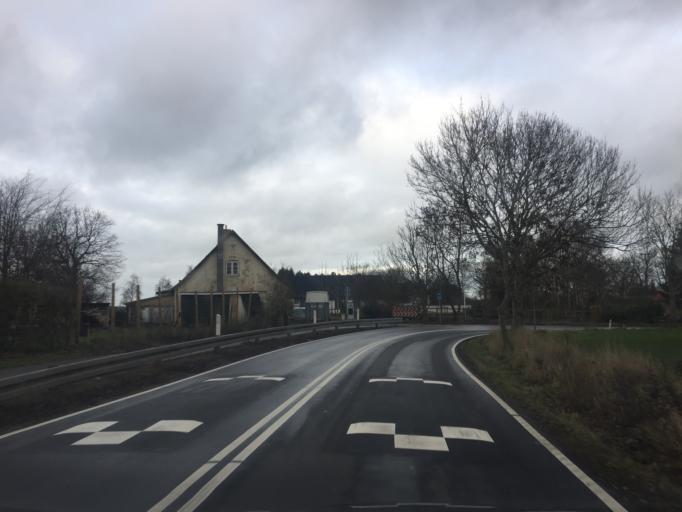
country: DK
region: Zealand
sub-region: Holbaek Kommune
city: Tollose
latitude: 55.6066
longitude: 11.7080
